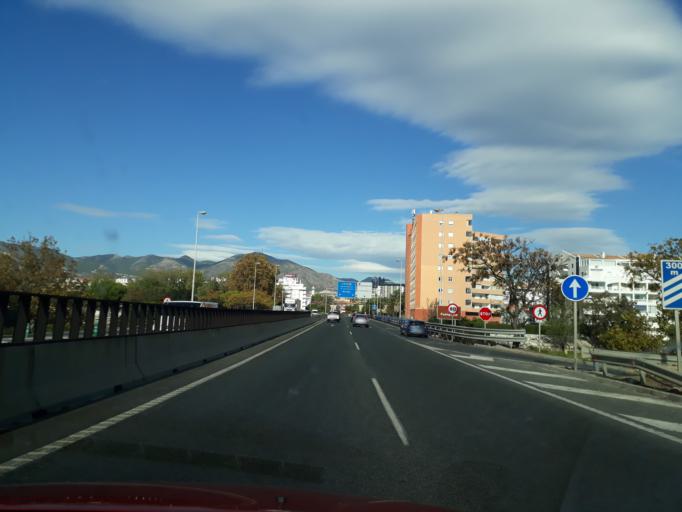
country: ES
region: Andalusia
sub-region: Provincia de Malaga
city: Fuengirola
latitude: 36.5264
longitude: -4.6297
